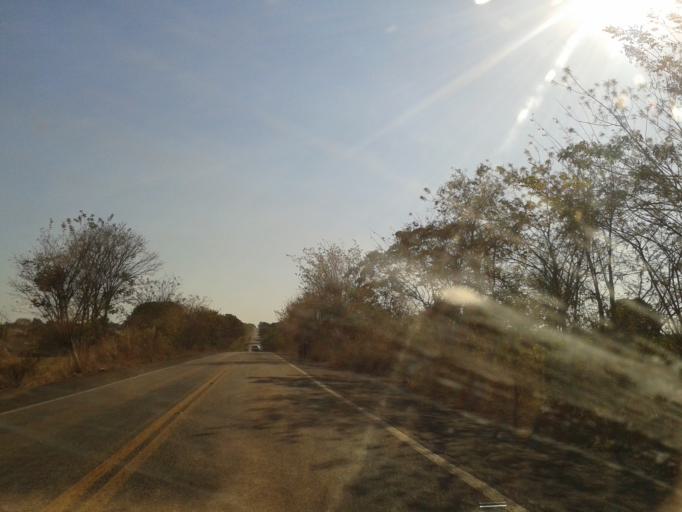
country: BR
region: Goias
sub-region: Mozarlandia
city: Mozarlandia
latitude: -15.0715
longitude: -50.6186
